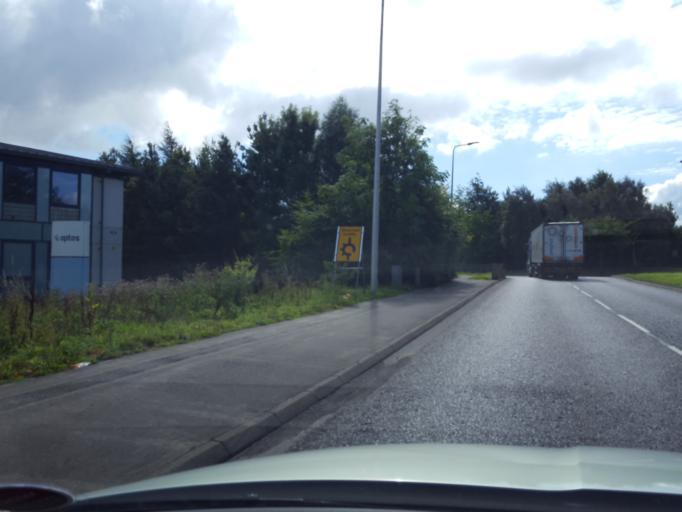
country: GB
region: Scotland
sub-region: Fife
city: Rosyth
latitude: 56.0484
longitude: -3.4300
